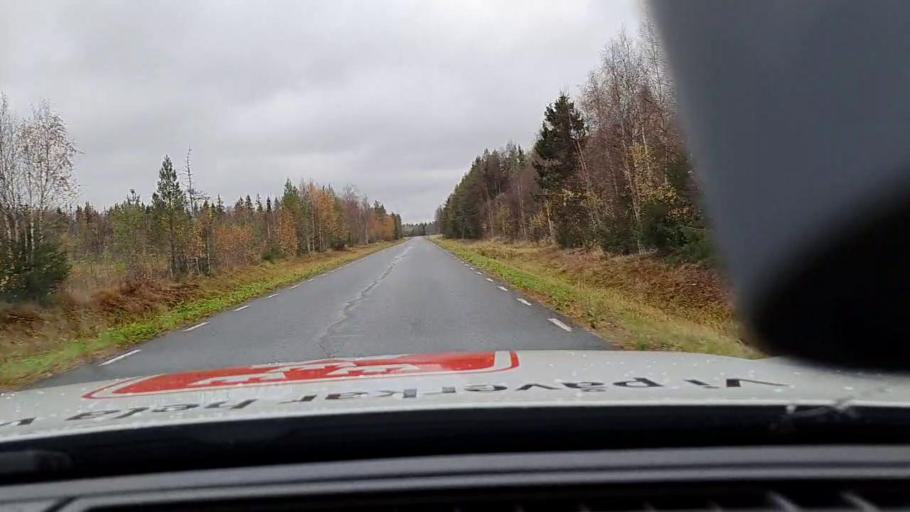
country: SE
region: Norrbotten
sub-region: Haparanda Kommun
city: Haparanda
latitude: 65.9280
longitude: 23.8182
